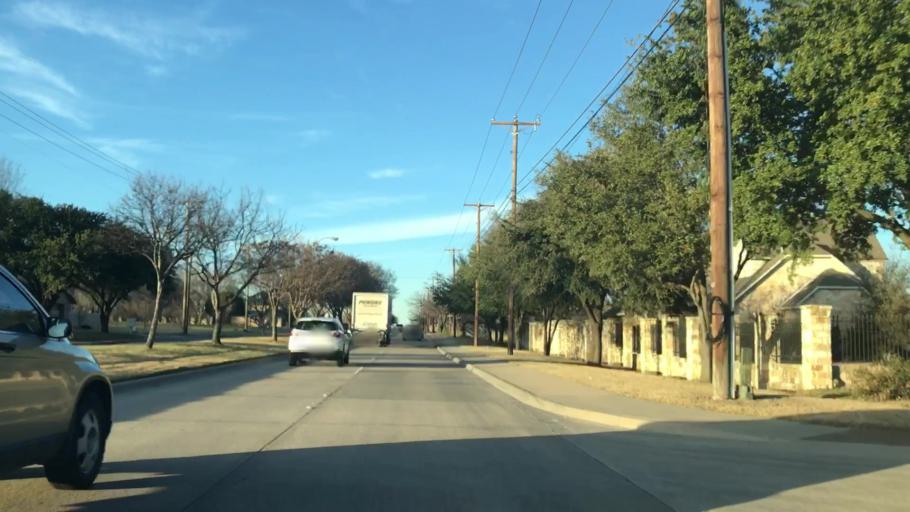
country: US
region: Texas
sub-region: Dallas County
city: Rowlett
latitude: 32.8828
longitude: -96.5182
